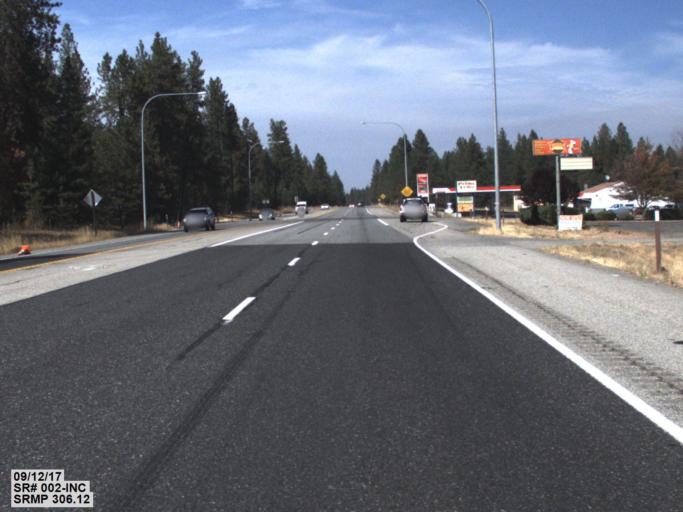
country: US
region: Washington
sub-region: Spokane County
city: Deer Park
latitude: 47.9130
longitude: -117.3502
